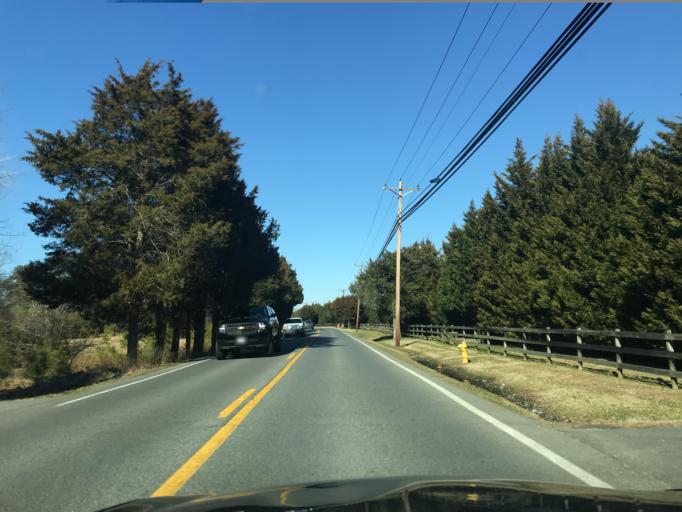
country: US
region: Maryland
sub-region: Charles County
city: Bennsville
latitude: 38.6318
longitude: -77.0150
